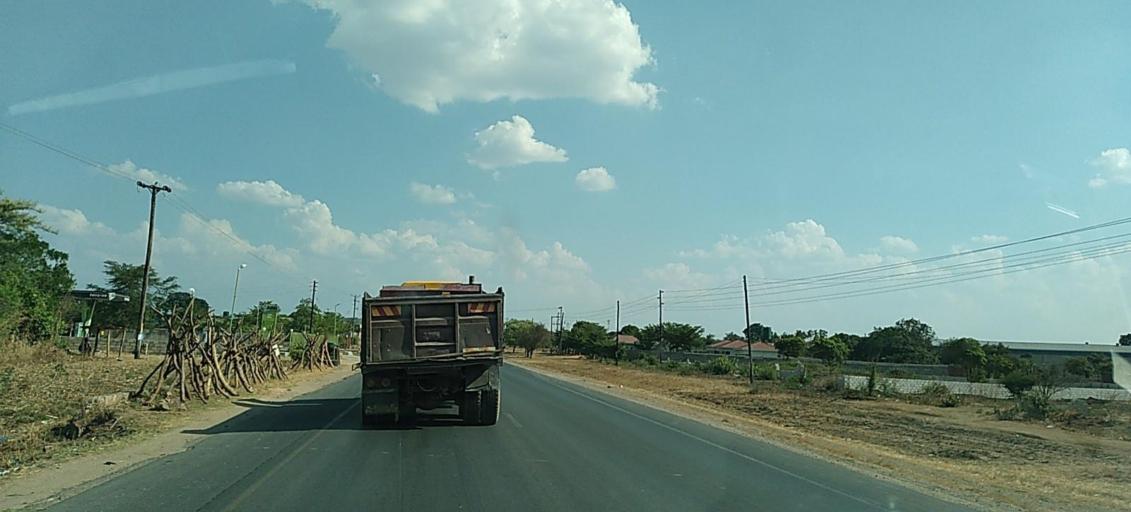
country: ZM
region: Lusaka
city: Lusaka
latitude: -15.2362
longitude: 28.2567
